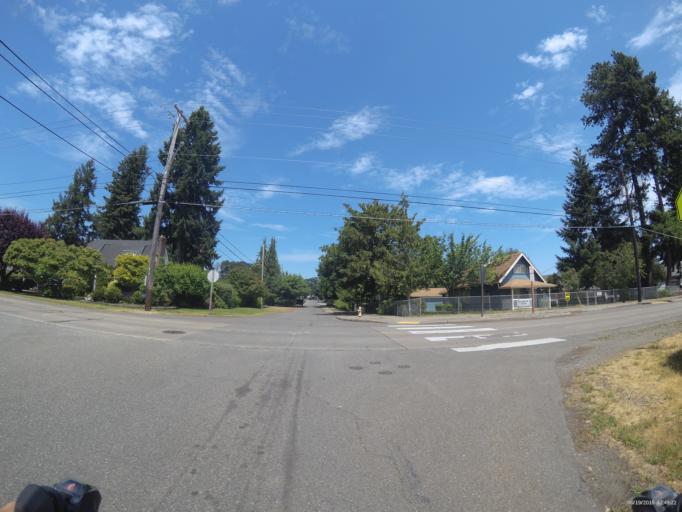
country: US
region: Washington
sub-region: Pierce County
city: Lakewood
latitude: 47.1650
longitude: -122.5232
